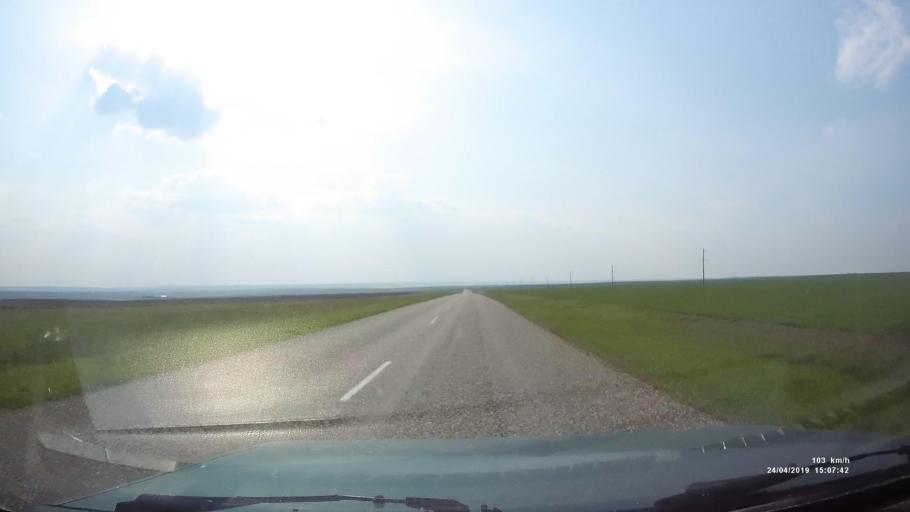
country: RU
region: Rostov
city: Remontnoye
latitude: 46.5598
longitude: 43.3991
